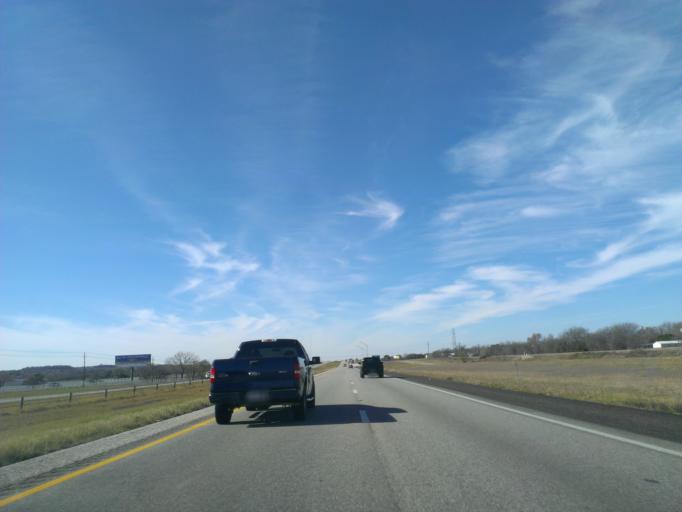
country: US
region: Texas
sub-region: Bell County
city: Nolanville
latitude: 31.0732
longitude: -97.5969
